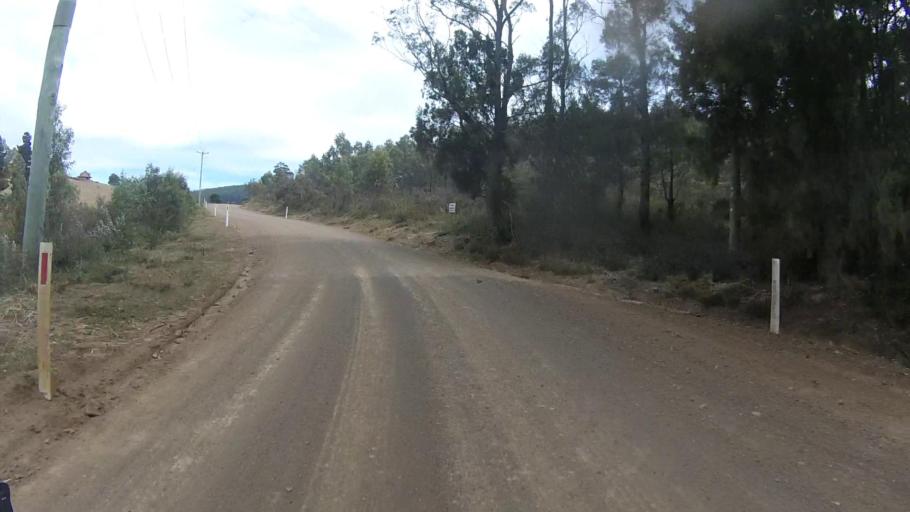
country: AU
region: Tasmania
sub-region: Sorell
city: Sorell
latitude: -42.7594
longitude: 147.8018
